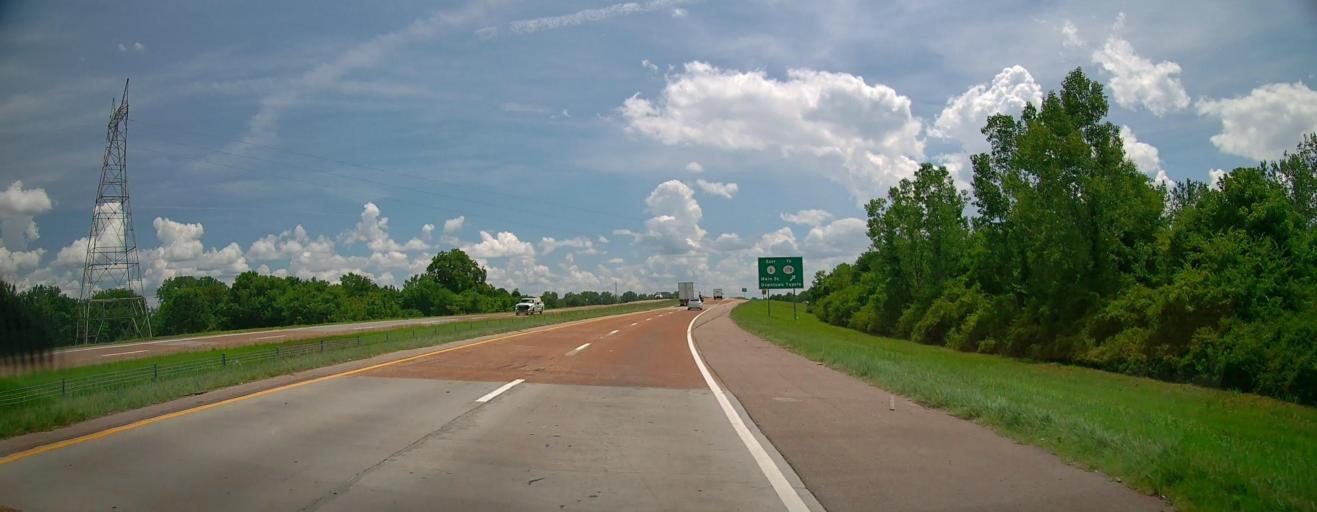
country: US
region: Mississippi
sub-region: Lee County
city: Tupelo
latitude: 34.2649
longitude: -88.6941
